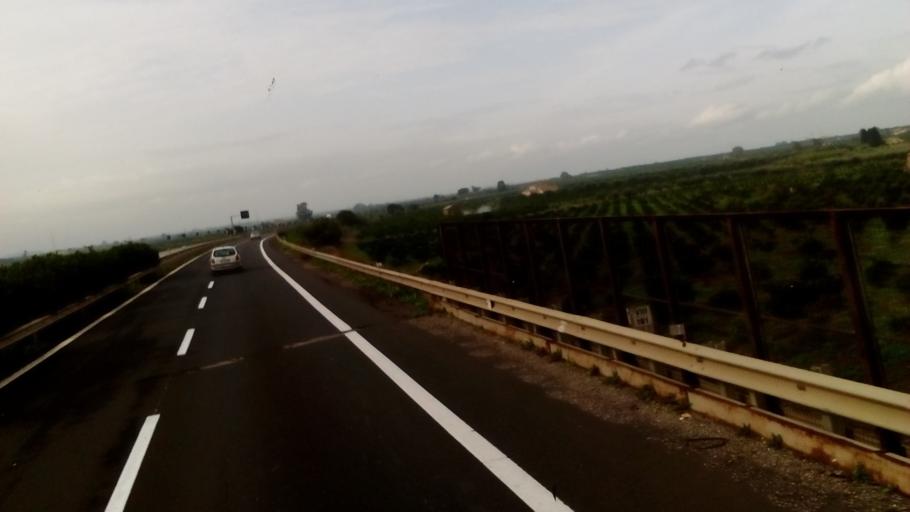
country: IT
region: Sicily
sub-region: Catania
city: Motta Sant'Anastasia
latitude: 37.4640
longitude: 14.9290
